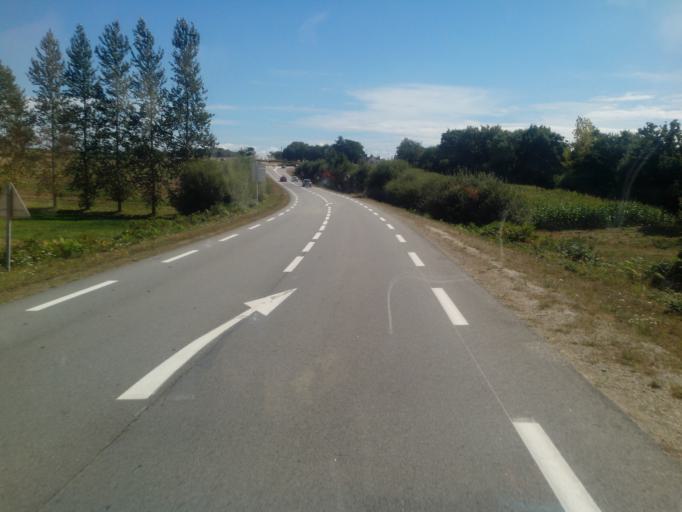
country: FR
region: Brittany
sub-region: Departement du Morbihan
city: Peaule
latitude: 47.5423
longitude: -2.3997
